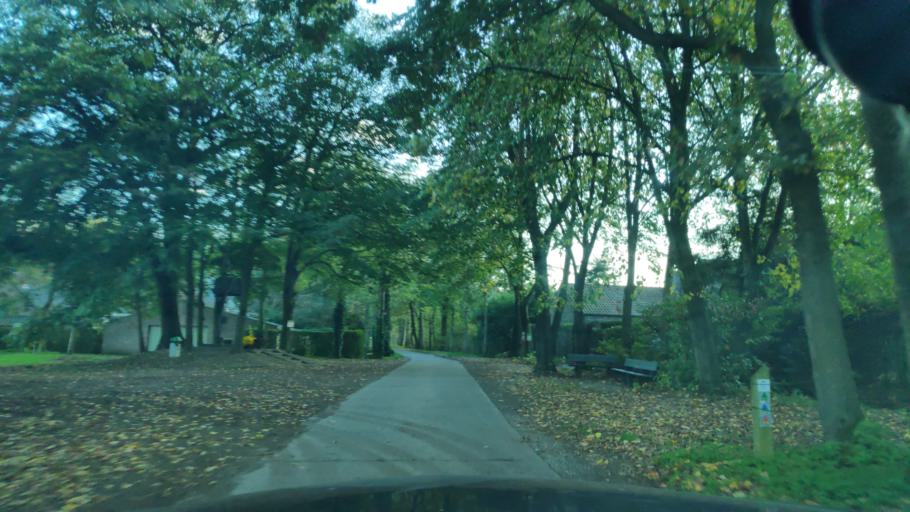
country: BE
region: Flanders
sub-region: Provincie Oost-Vlaanderen
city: Zomergem
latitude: 51.1374
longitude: 3.5074
